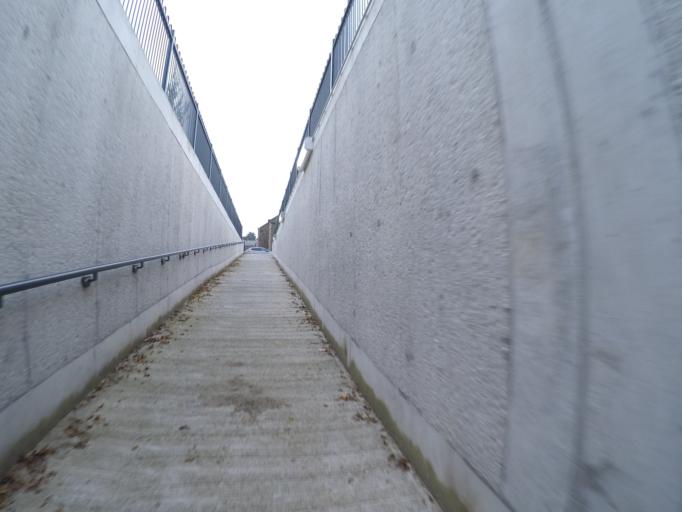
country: BE
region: Wallonia
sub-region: Province de Namur
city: Ciney
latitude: 50.3171
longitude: 5.0676
